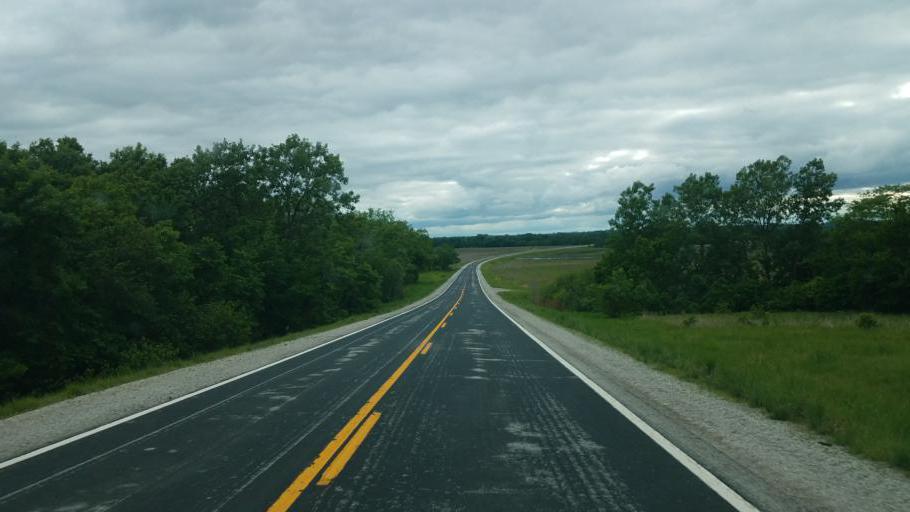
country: US
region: Missouri
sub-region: Mercer County
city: Princeton
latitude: 40.3389
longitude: -93.7513
